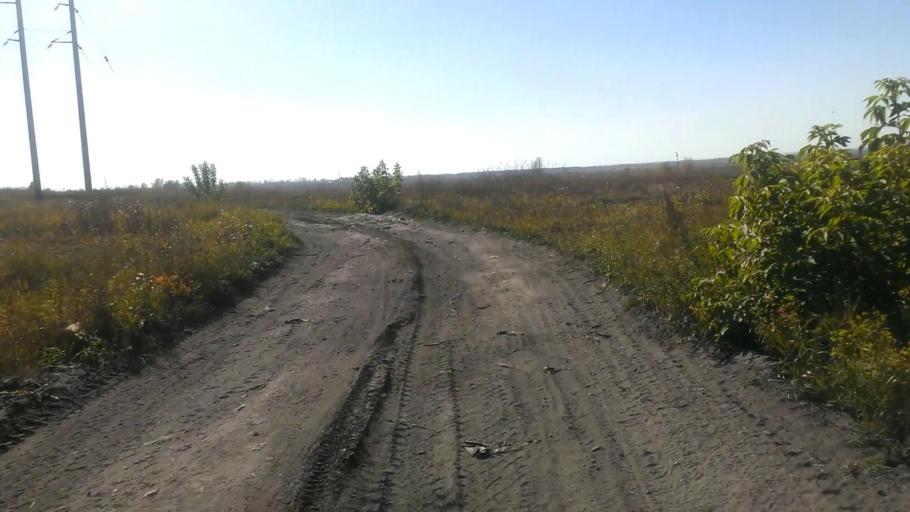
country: RU
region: Altai Krai
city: Novoaltaysk
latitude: 53.3663
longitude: 83.9454
